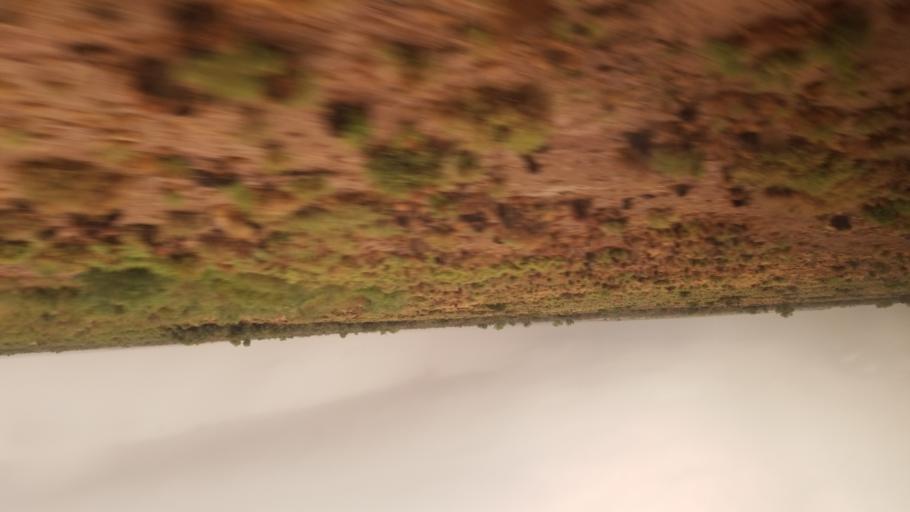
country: US
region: Arizona
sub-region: Navajo County
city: Joseph City
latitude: 34.9674
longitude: -110.4392
